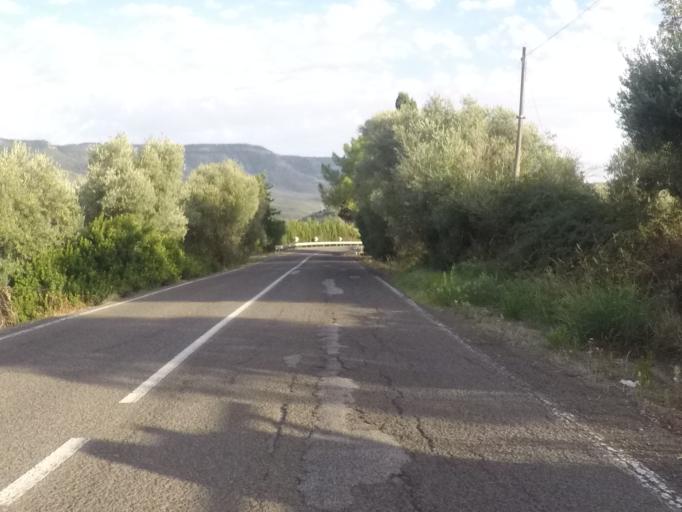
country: IT
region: Sardinia
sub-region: Provincia di Sassari
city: Alghero
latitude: 40.5108
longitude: 8.3559
